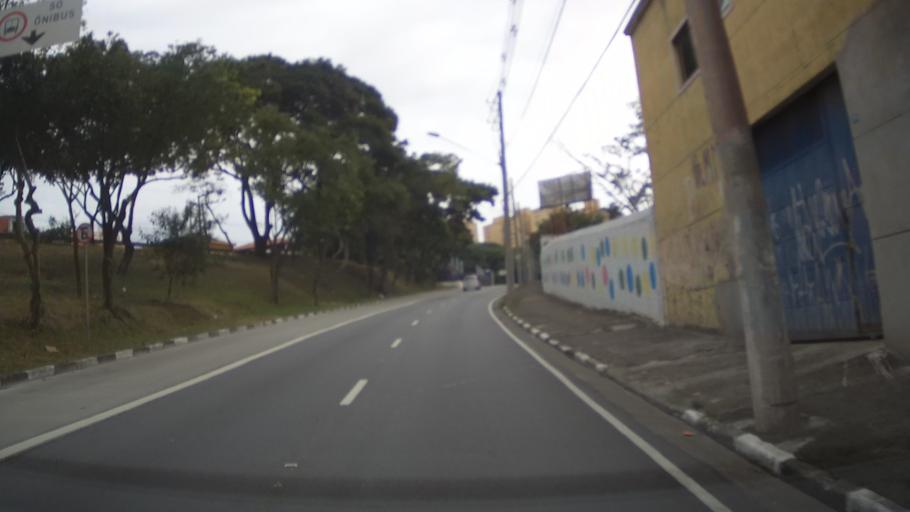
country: BR
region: Sao Paulo
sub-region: Guarulhos
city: Guarulhos
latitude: -23.4562
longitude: -46.5543
